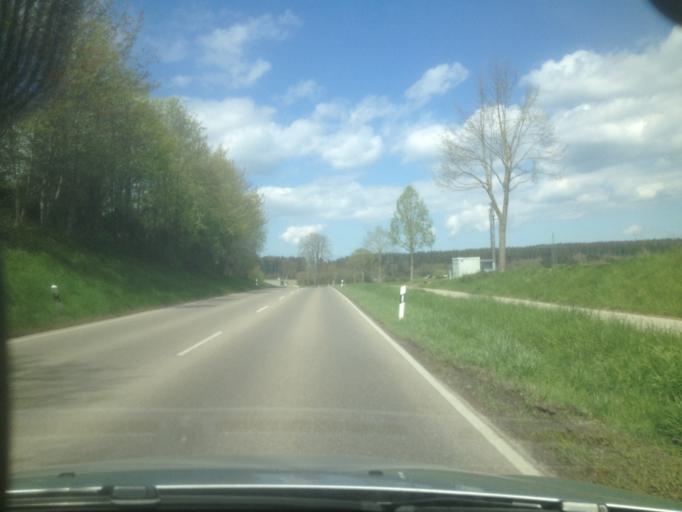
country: DE
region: Bavaria
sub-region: Swabia
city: Aystetten
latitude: 48.3791
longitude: 10.7566
